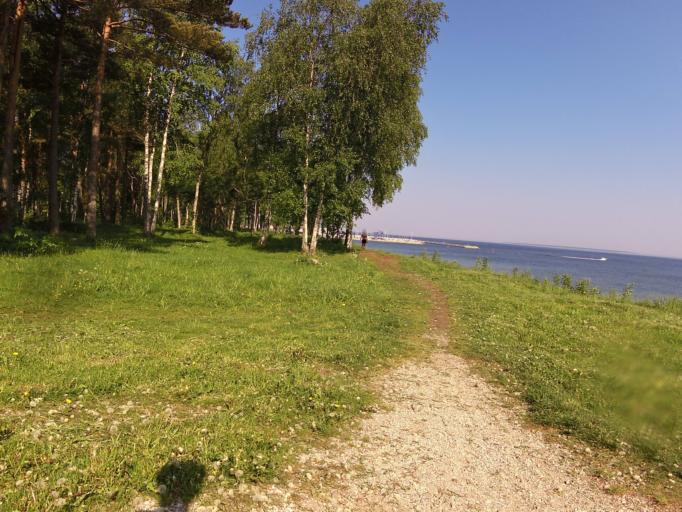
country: EE
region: Harju
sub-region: Harku vald
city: Tabasalu
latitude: 59.4465
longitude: 24.6149
